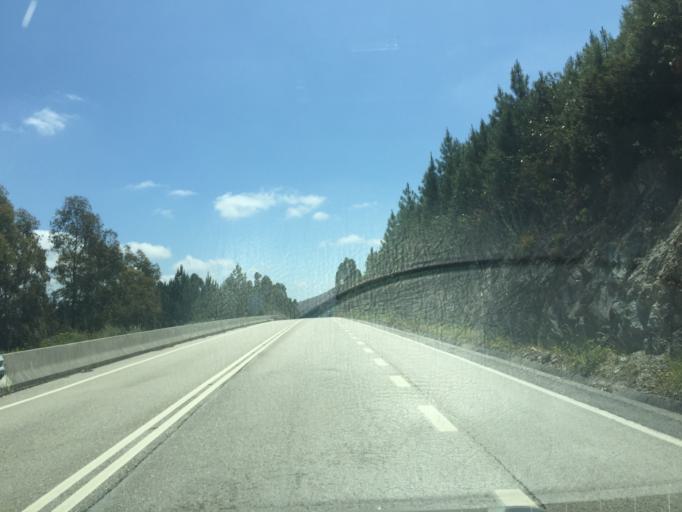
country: PT
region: Castelo Branco
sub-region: Vila de Rei
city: Vila de Rei
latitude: 39.7102
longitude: -8.1392
